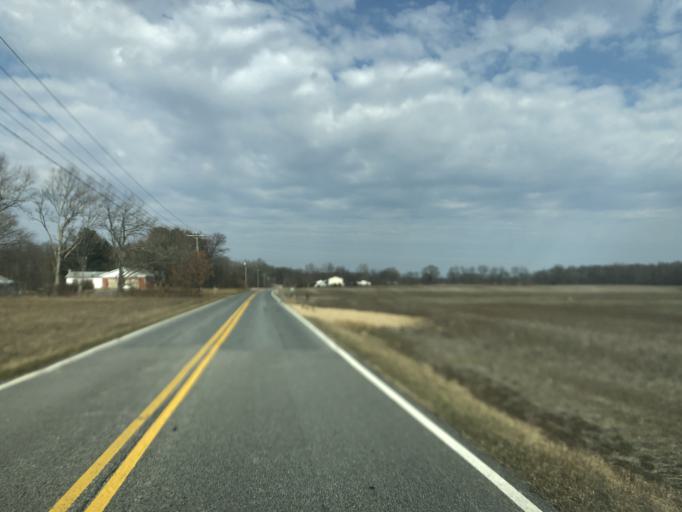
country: US
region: Maryland
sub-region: Caroline County
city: Ridgely
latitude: 39.0678
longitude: -75.9290
